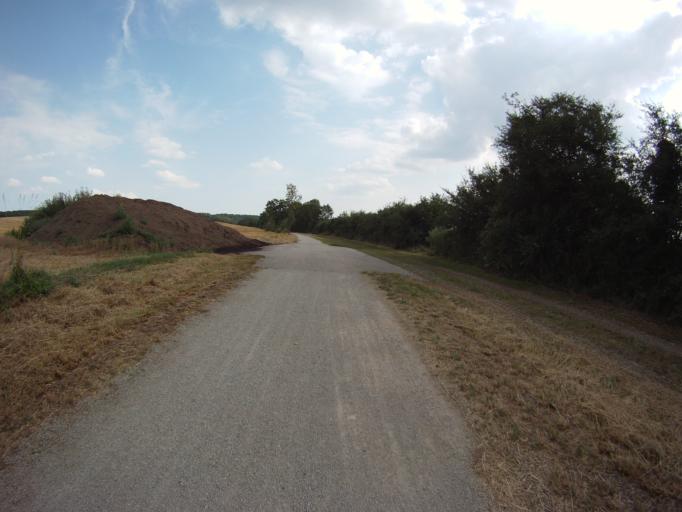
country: FR
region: Lorraine
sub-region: Departement de la Moselle
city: Courcelles-Chaussy
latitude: 49.1265
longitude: 6.3841
